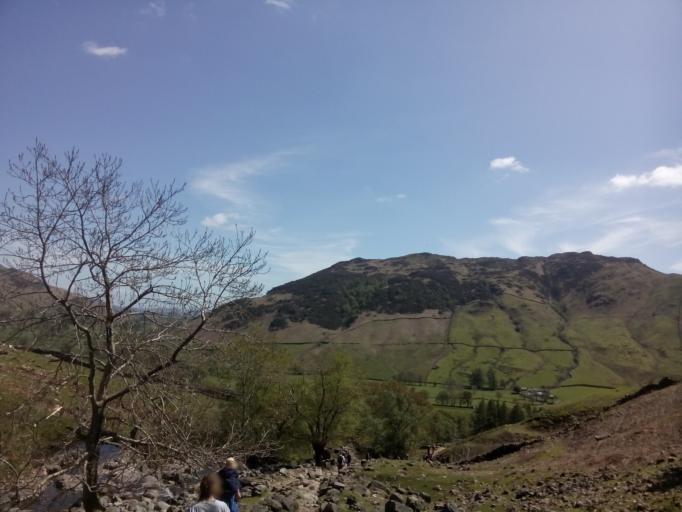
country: GB
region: England
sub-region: Cumbria
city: Ambleside
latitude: 54.4513
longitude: -3.0931
